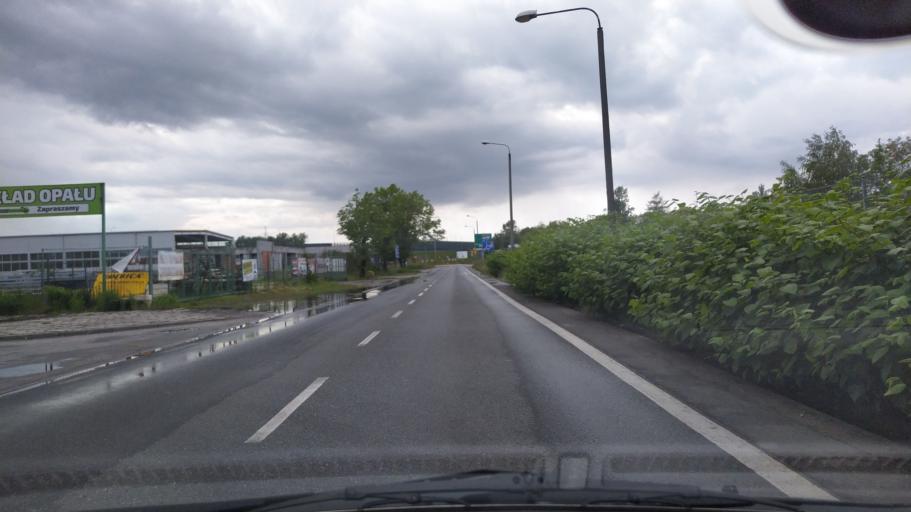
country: PL
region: Silesian Voivodeship
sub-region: Gliwice
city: Gliwice
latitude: 50.2899
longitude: 18.7058
